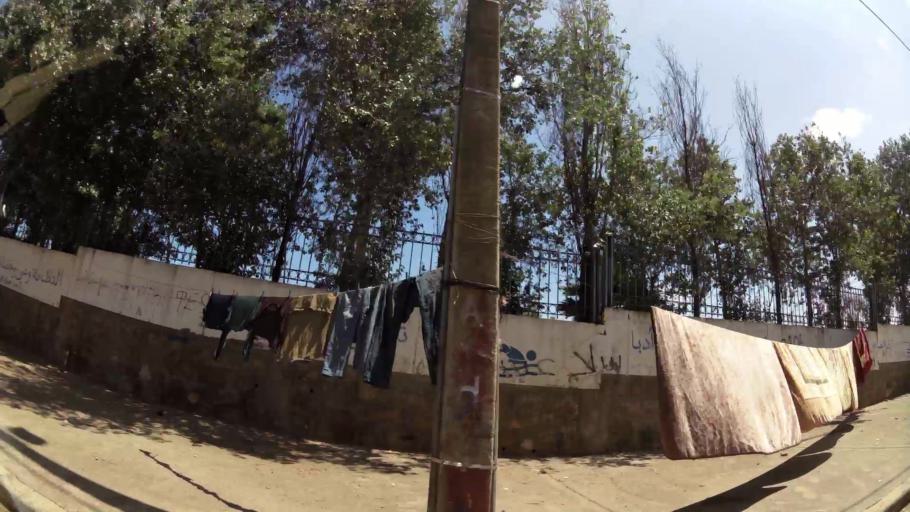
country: MA
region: Rabat-Sale-Zemmour-Zaer
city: Sale
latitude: 34.0704
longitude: -6.7828
